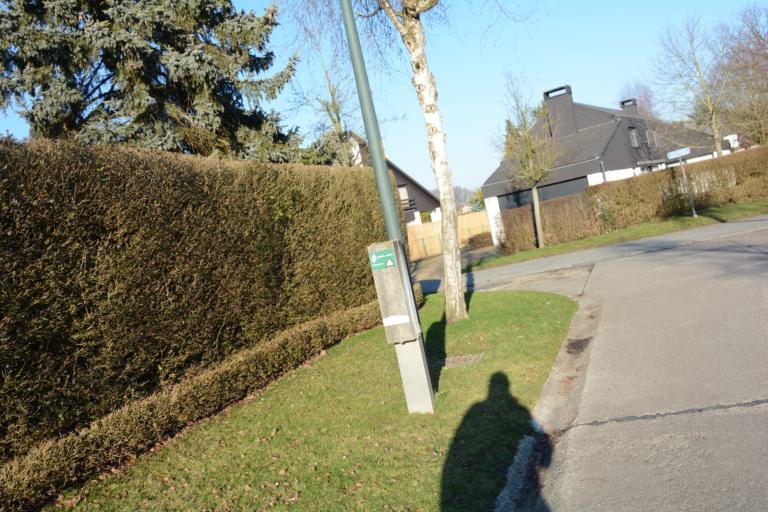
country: BE
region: Flanders
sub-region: Provincie Vlaams-Brabant
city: Bever
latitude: 50.9212
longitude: 4.3206
